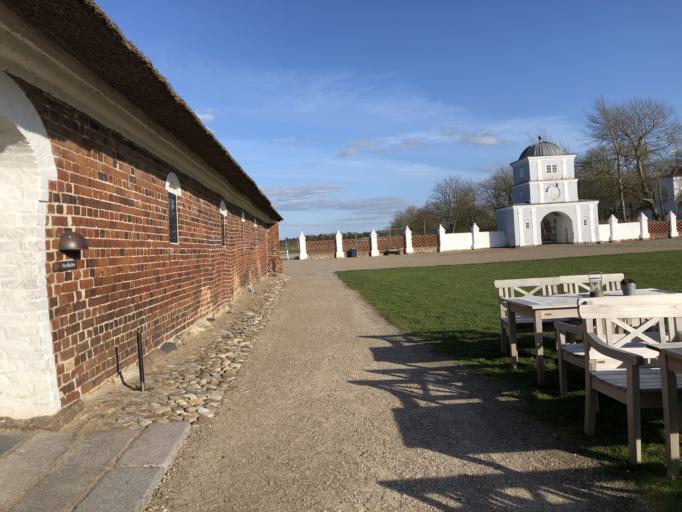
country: DK
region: Central Jutland
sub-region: Holstebro Kommune
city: Ulfborg
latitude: 56.3266
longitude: 8.3313
